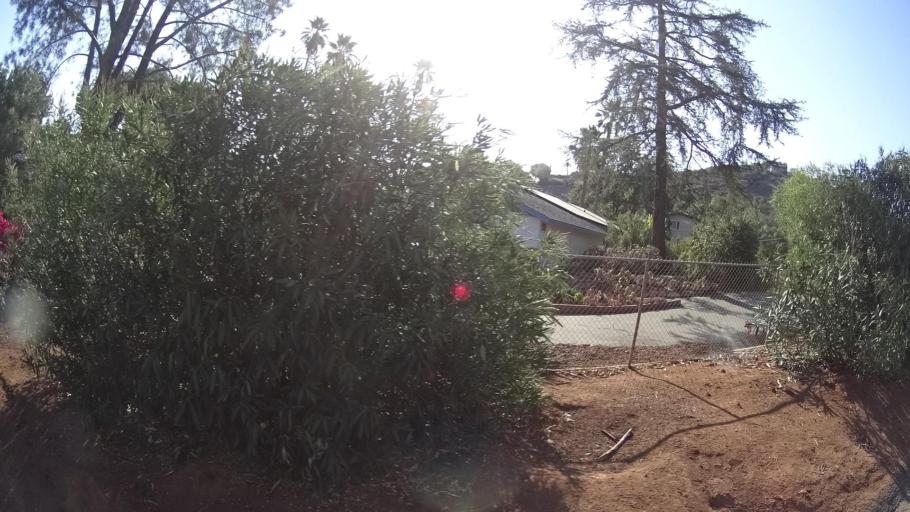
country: US
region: California
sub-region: San Diego County
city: Eucalyptus Hills
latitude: 32.8954
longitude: -116.9426
